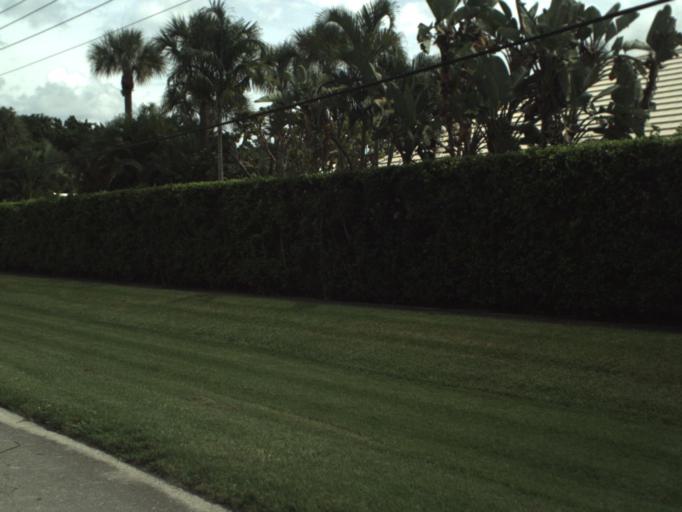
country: US
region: Florida
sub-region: Palm Beach County
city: Juno Beach
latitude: 26.8416
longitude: -80.0505
